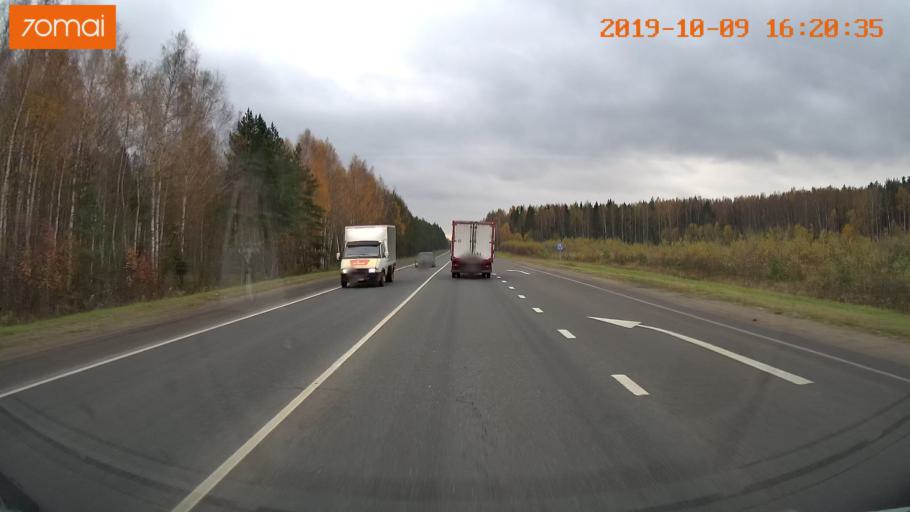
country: RU
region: Kostroma
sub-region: Kostromskoy Rayon
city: Kostroma
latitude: 57.7047
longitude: 40.8918
